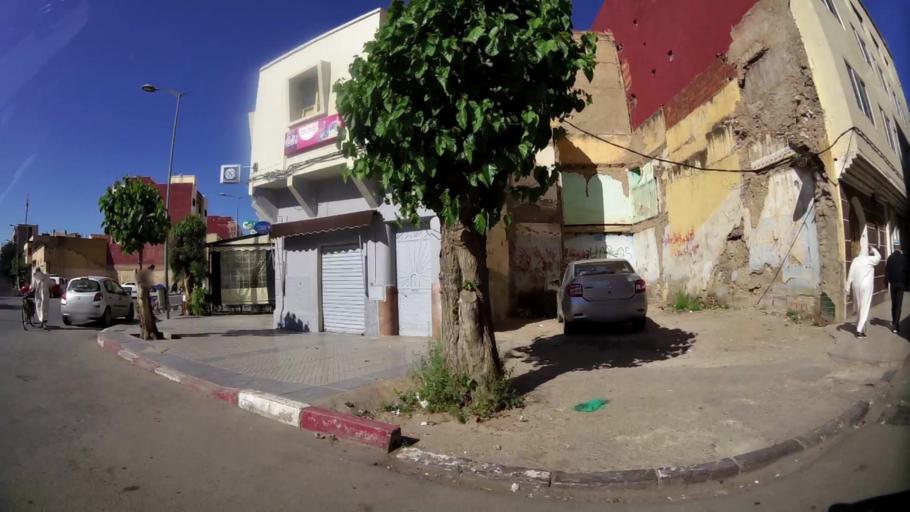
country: MA
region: Oriental
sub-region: Oujda-Angad
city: Oujda
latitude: 34.6860
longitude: -1.9164
